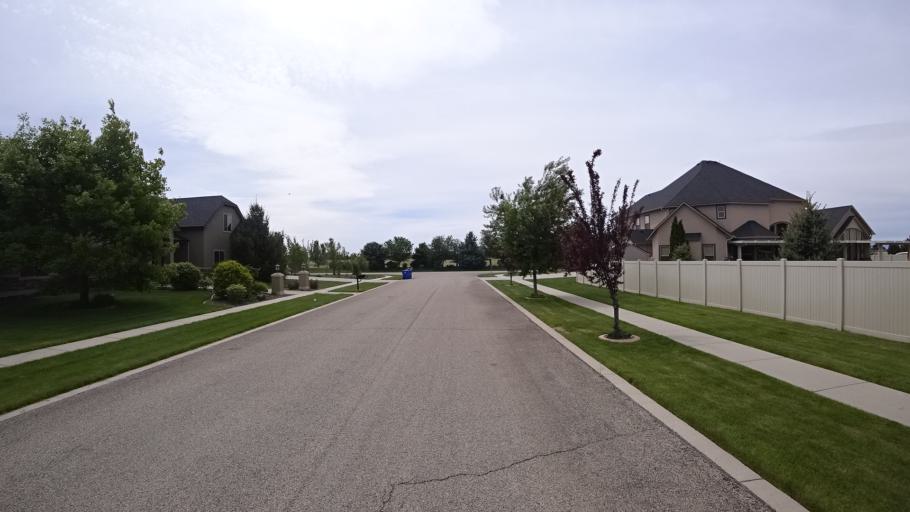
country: US
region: Idaho
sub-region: Ada County
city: Kuna
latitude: 43.5389
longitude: -116.4010
